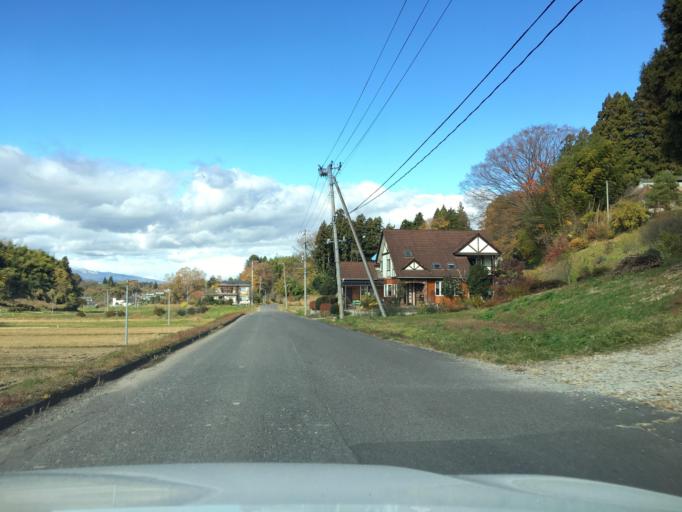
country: JP
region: Fukushima
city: Miharu
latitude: 37.5025
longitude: 140.4964
